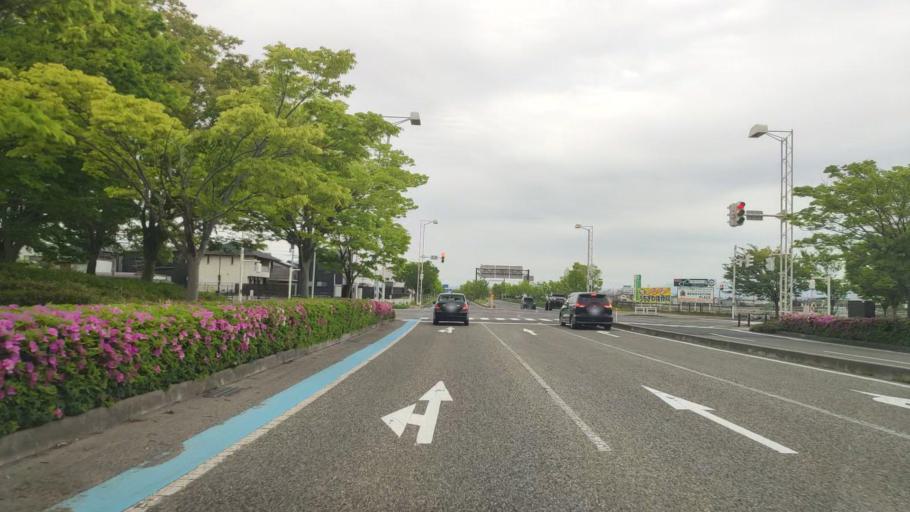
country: JP
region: Niigata
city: Niigata-shi
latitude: 37.8819
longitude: 139.0641
